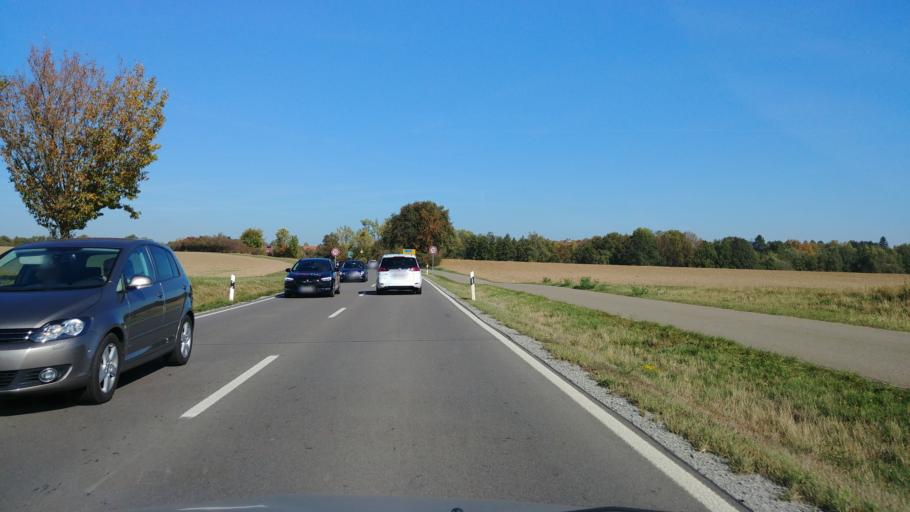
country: DE
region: Baden-Wuerttemberg
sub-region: Regierungsbezirk Stuttgart
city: Schwaebisch Hall
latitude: 49.0938
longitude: 9.7187
